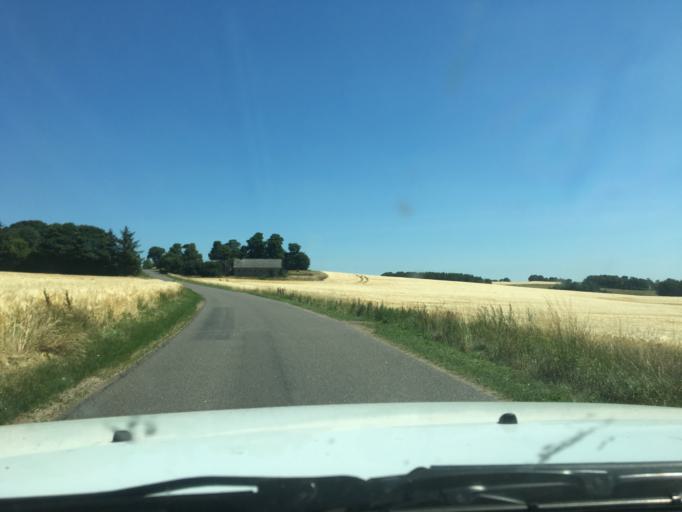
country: DK
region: Central Jutland
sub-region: Horsens Kommune
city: Braedstrup
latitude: 55.9398
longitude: 9.5512
